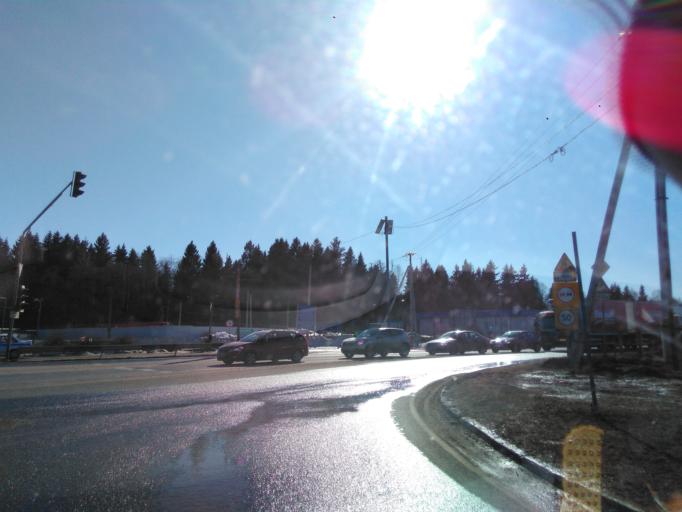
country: RU
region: Moskovskaya
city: Yermolino
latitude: 56.1387
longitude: 37.4951
